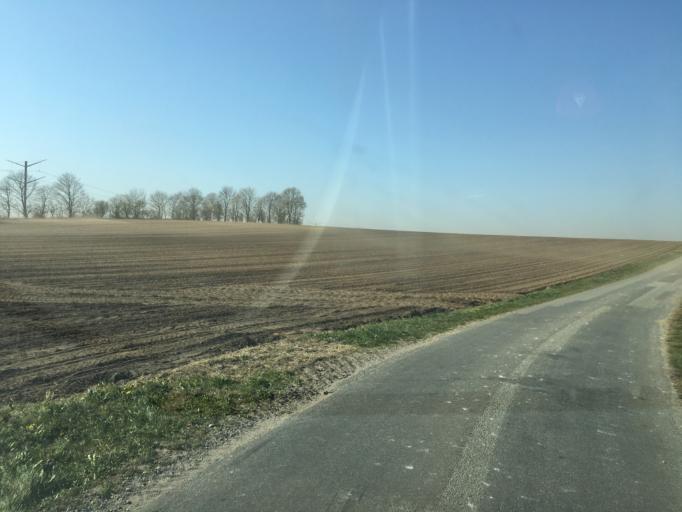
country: DK
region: South Denmark
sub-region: Aabenraa Kommune
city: Rodekro
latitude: 55.1083
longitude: 9.2195
